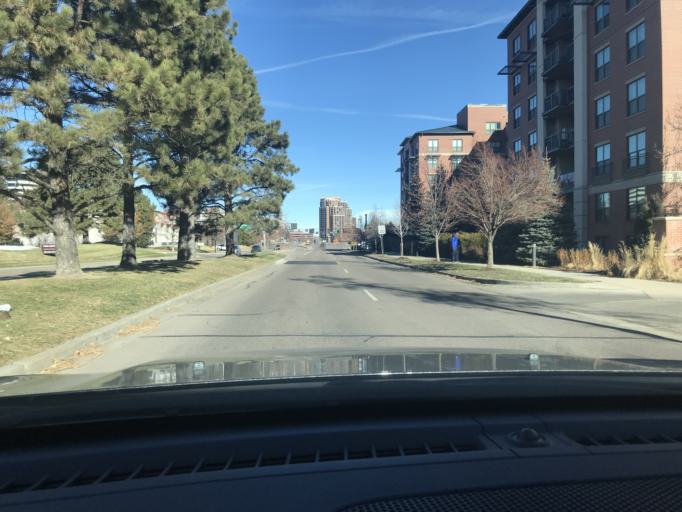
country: US
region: Colorado
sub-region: Arapahoe County
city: Castlewood
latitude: 39.6212
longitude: -104.8947
